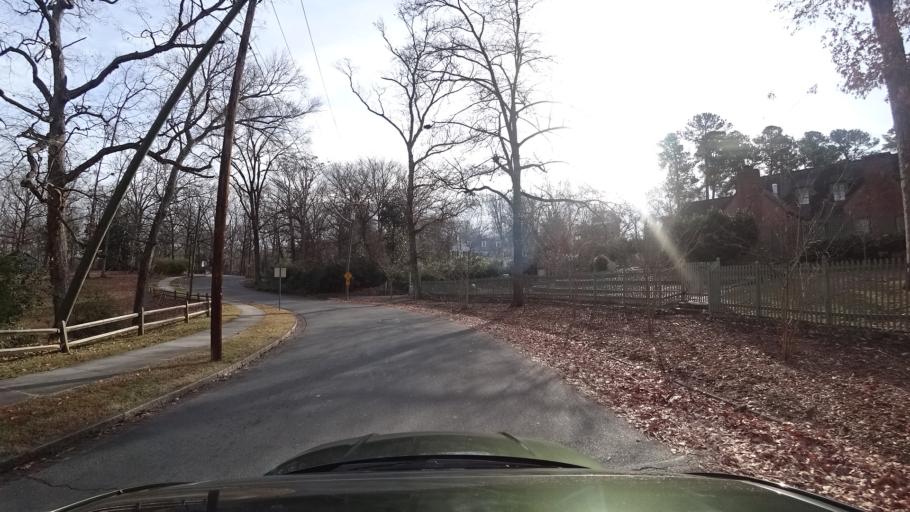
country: US
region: North Carolina
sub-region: Durham County
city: Durham
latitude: 36.0126
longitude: -78.8943
